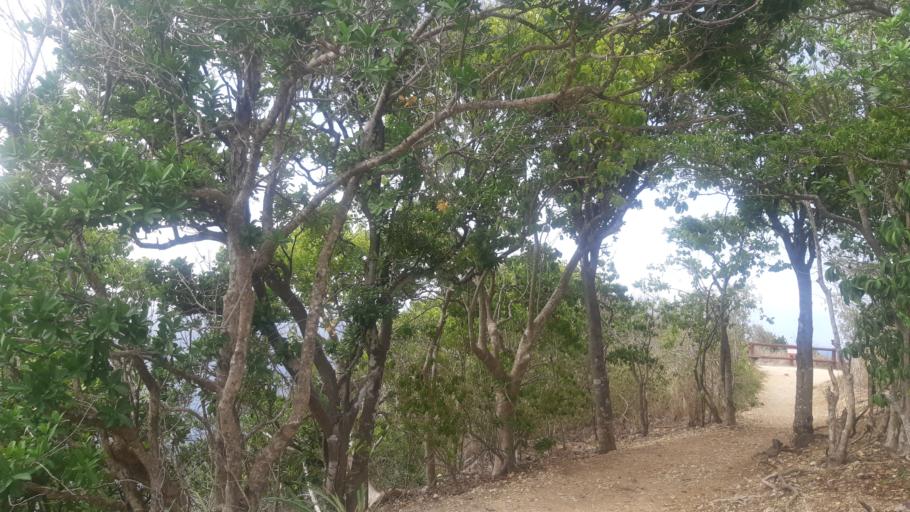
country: GP
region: Guadeloupe
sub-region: Guadeloupe
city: Anse-Bertrand
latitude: 16.5115
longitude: -61.4654
